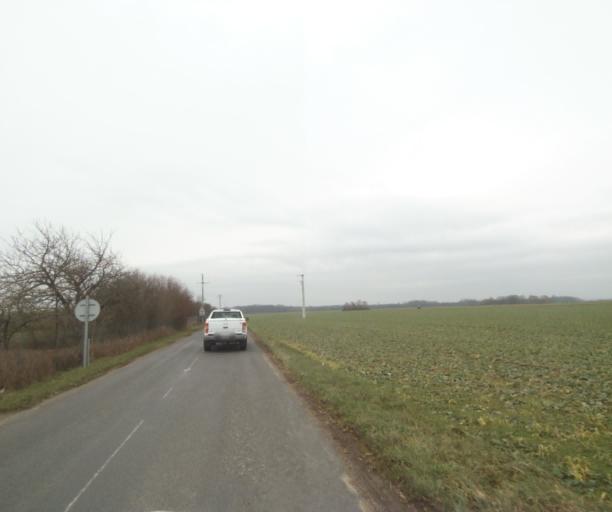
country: FR
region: Champagne-Ardenne
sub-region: Departement de la Haute-Marne
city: Villiers-en-Lieu
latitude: 48.6650
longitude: 4.8919
